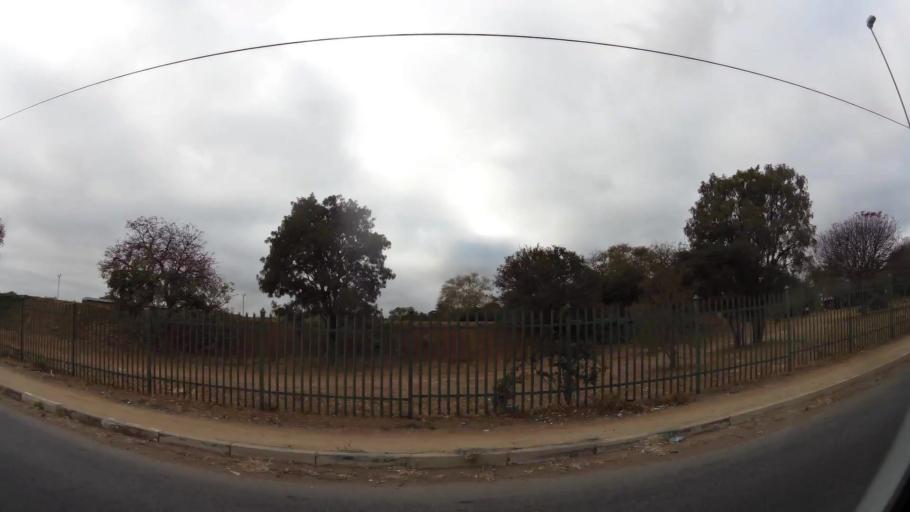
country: ZA
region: Limpopo
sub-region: Capricorn District Municipality
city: Polokwane
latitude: -23.8833
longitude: 29.4579
